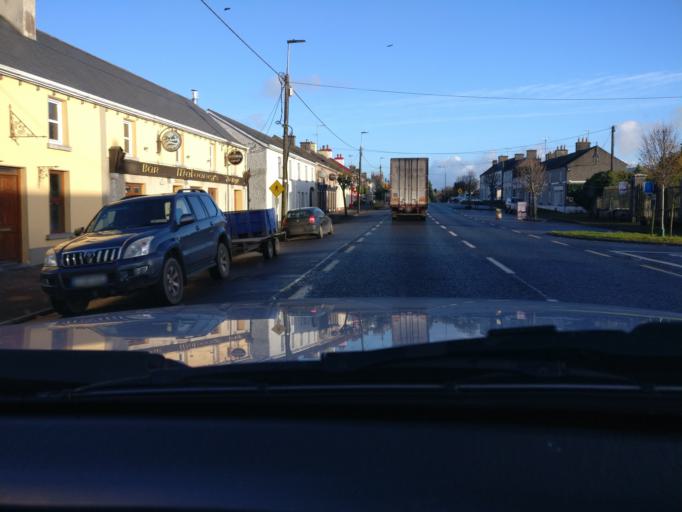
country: IE
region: Leinster
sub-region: An Mhi
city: Athboy
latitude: 53.6639
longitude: -7.0168
